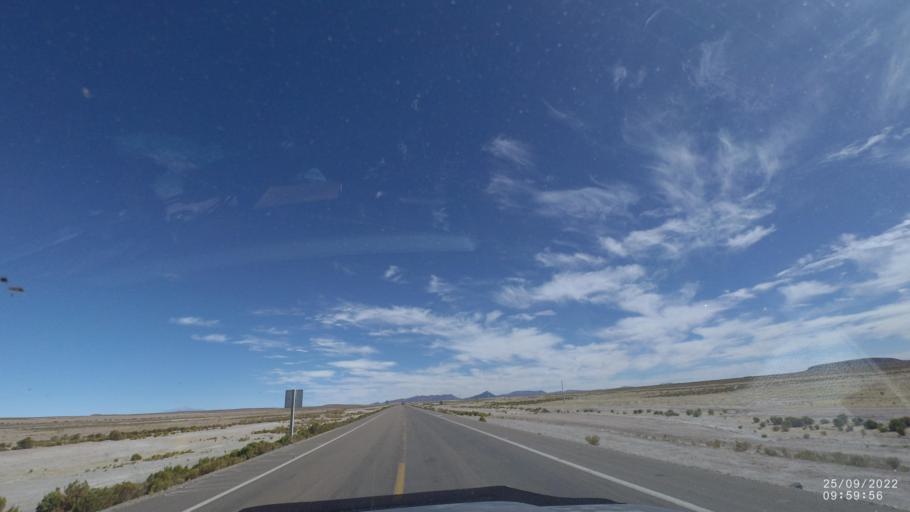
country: BO
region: Potosi
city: Colchani
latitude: -20.2827
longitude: -66.9421
